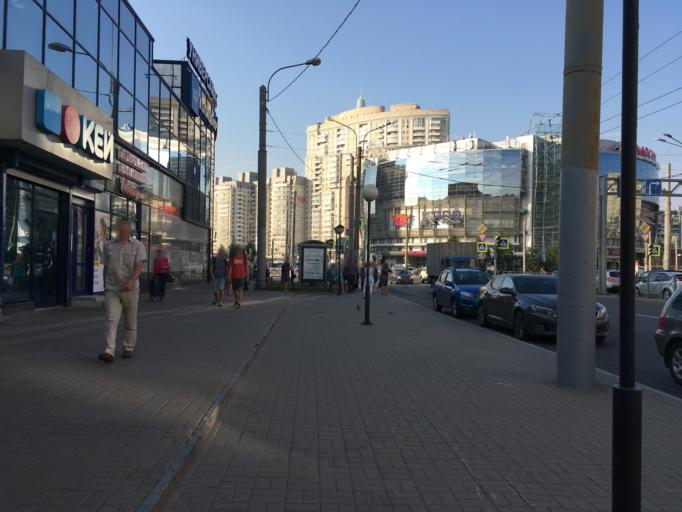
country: RU
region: St.-Petersburg
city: Komendantsky aerodrom
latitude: 60.0063
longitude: 30.2580
